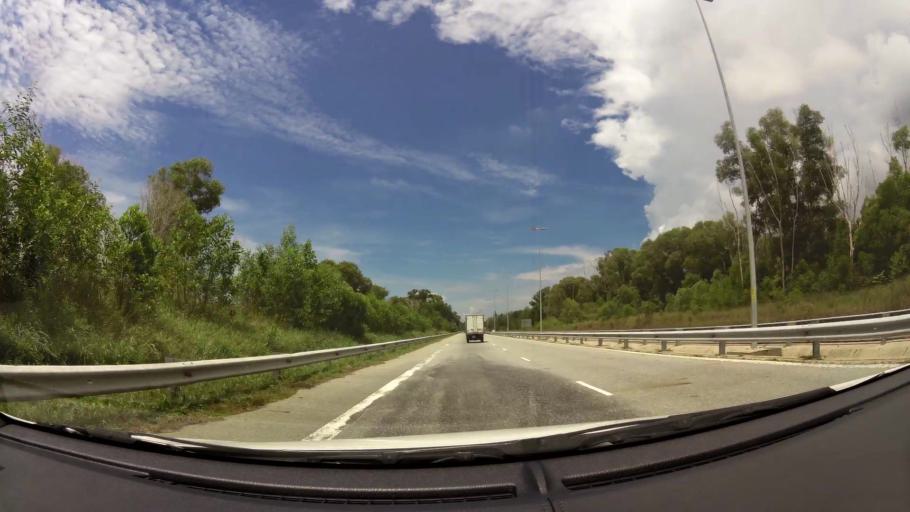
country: BN
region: Brunei and Muara
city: Bandar Seri Begawan
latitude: 4.9768
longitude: 114.8862
